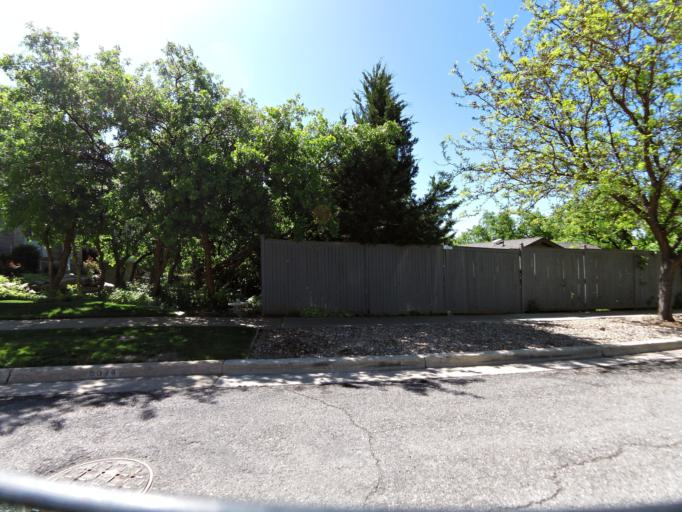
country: US
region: Utah
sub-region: Weber County
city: Uintah
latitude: 41.1720
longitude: -111.9314
